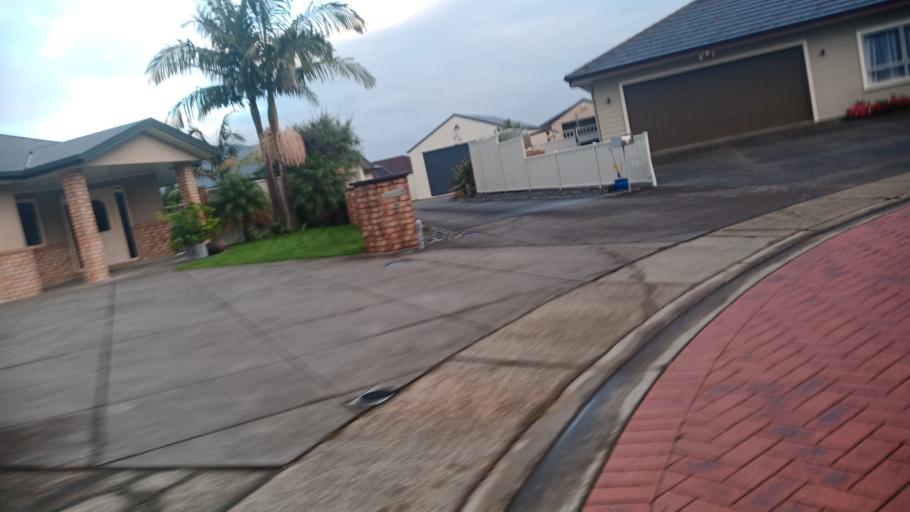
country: NZ
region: Gisborne
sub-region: Gisborne District
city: Gisborne
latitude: -38.6386
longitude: 177.9979
